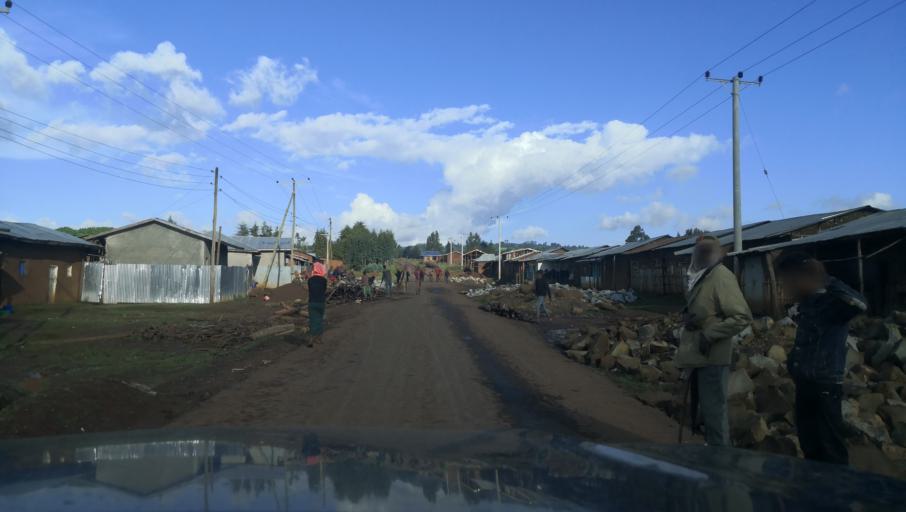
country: ET
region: Oromiya
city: Tulu Bolo
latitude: 8.3928
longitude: 38.2879
